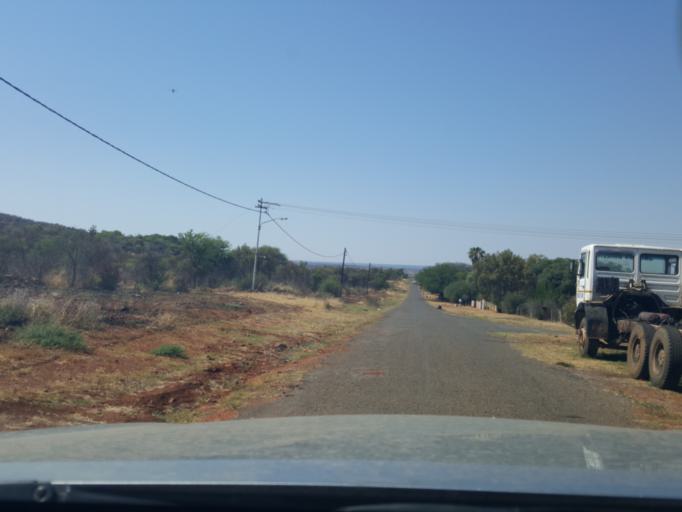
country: ZA
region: North-West
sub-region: Ngaka Modiri Molema District Municipality
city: Zeerust
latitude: -25.5264
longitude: 26.0802
